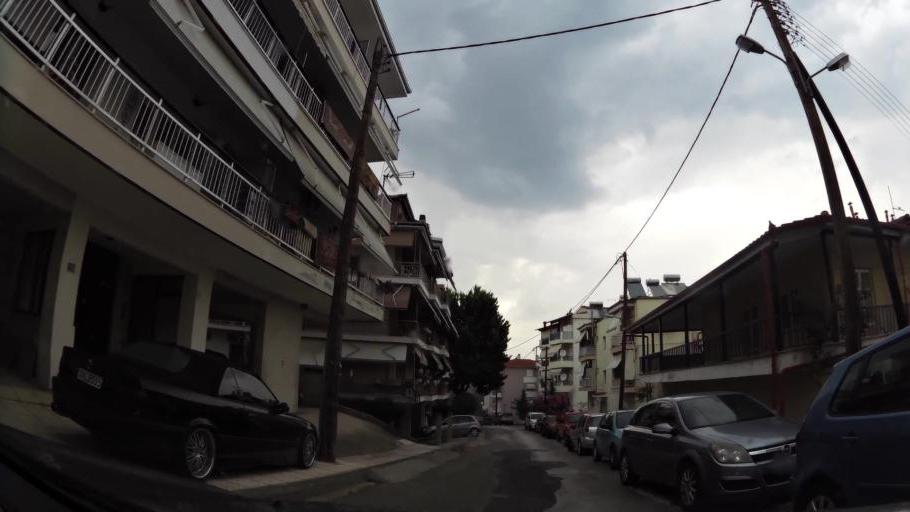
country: GR
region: Central Macedonia
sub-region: Nomos Imathias
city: Veroia
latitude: 40.5237
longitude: 22.1952
